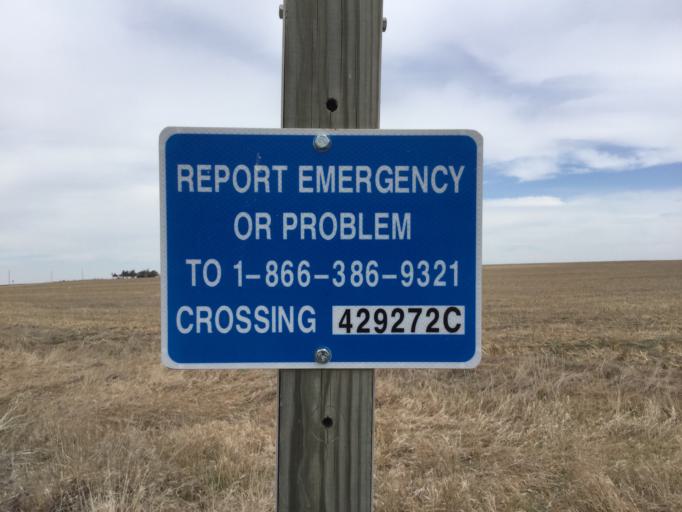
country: US
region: Kansas
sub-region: Barton County
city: Hoisington
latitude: 38.5070
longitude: -98.9023
